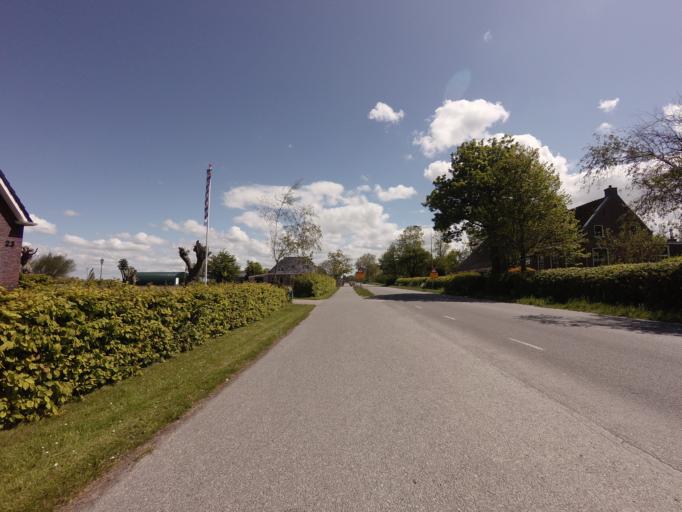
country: NL
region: Friesland
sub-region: Gemeente Harlingen
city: Harlingen
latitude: 53.1403
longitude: 5.4425
